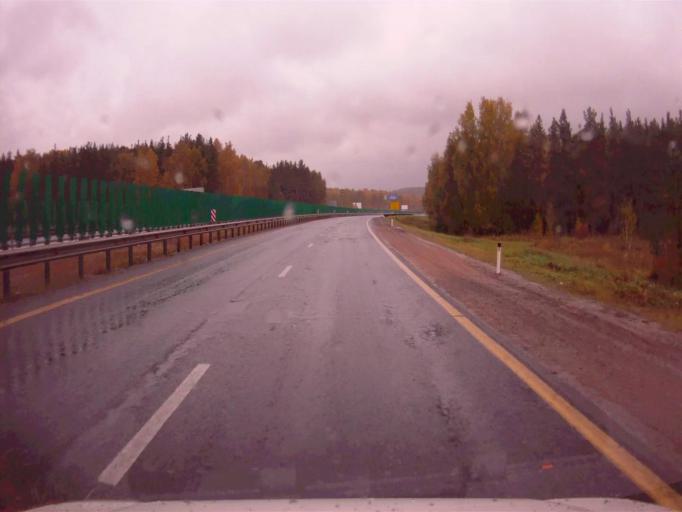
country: RU
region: Chelyabinsk
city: Dolgoderevenskoye
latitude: 55.3381
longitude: 61.3080
